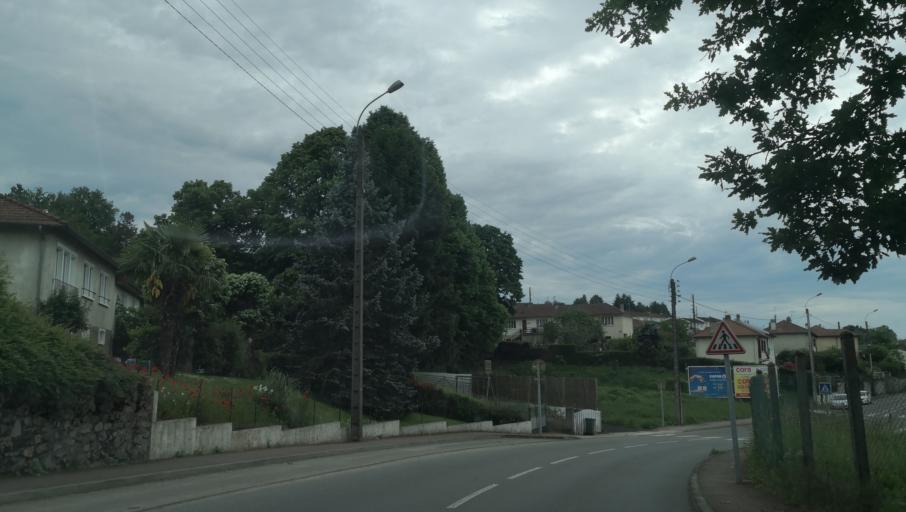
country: FR
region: Limousin
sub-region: Departement de la Haute-Vienne
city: Couzeix
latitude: 45.8584
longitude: 1.2534
